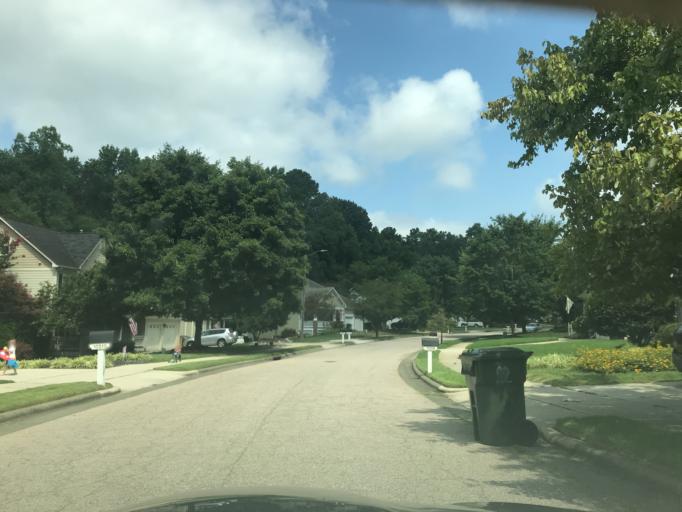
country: US
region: North Carolina
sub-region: Wake County
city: Wake Forest
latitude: 35.9141
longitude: -78.5682
